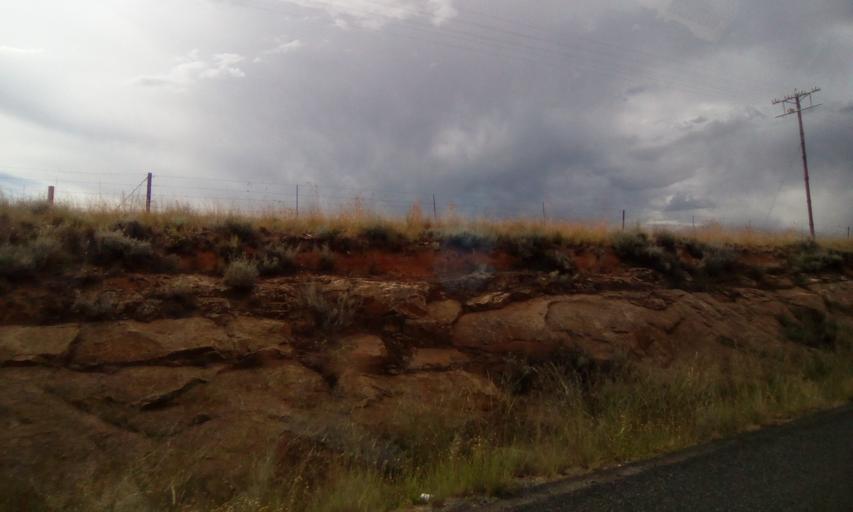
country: ZA
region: Orange Free State
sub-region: Thabo Mofutsanyana District Municipality
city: Ladybrand
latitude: -29.2346
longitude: 27.4495
